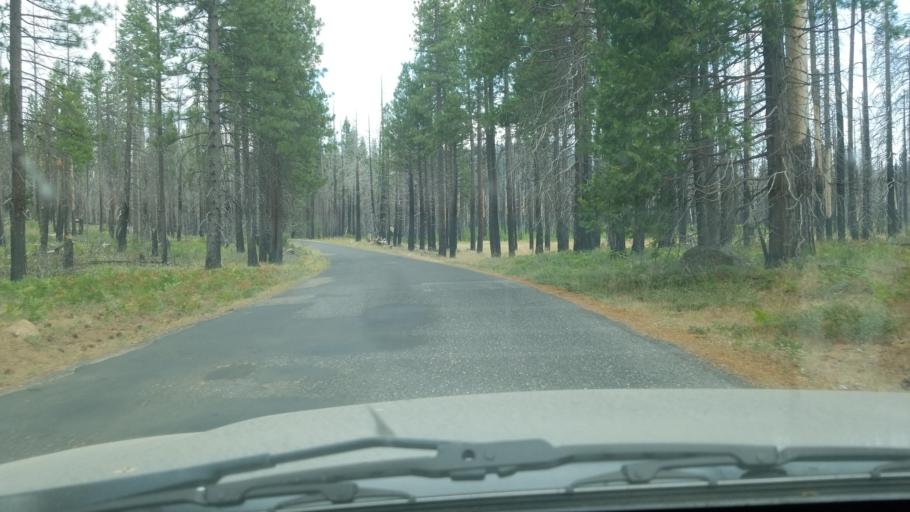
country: US
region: California
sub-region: Mariposa County
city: Yosemite Valley
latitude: 37.8398
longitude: -119.8524
